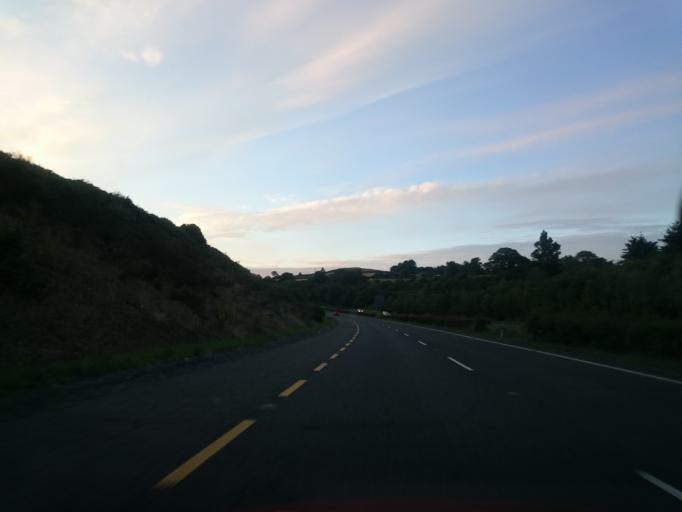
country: IE
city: Newtownmountkennedy
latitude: 53.0534
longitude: -6.0918
